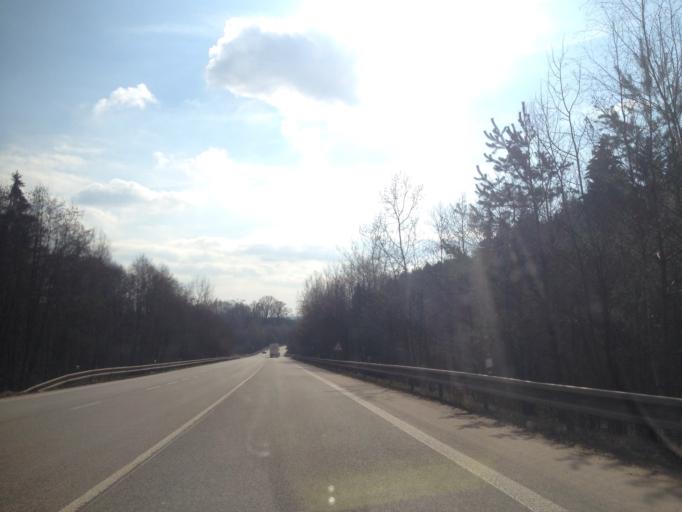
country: CZ
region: Kralovehradecky
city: Nova Paka
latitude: 50.4494
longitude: 15.4705
